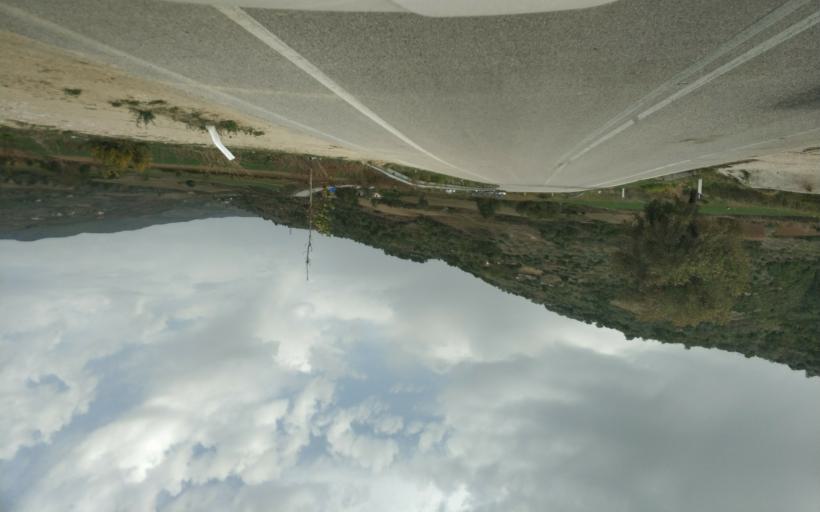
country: AL
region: Gjirokaster
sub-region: Rrethi i Tepelenes
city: Krahes
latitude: 40.4535
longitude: 19.8488
